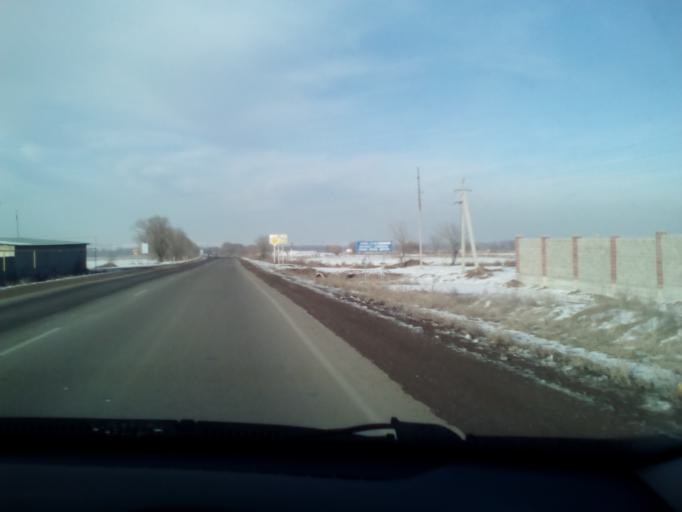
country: KZ
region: Almaty Oblysy
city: Burunday
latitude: 43.2052
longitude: 76.4150
